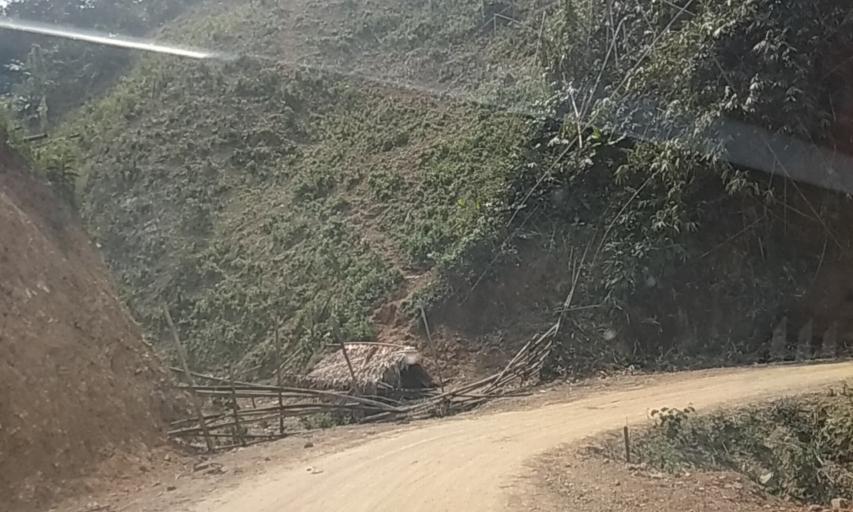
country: LA
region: Phongsali
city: Phongsali
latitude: 21.4724
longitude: 102.4343
